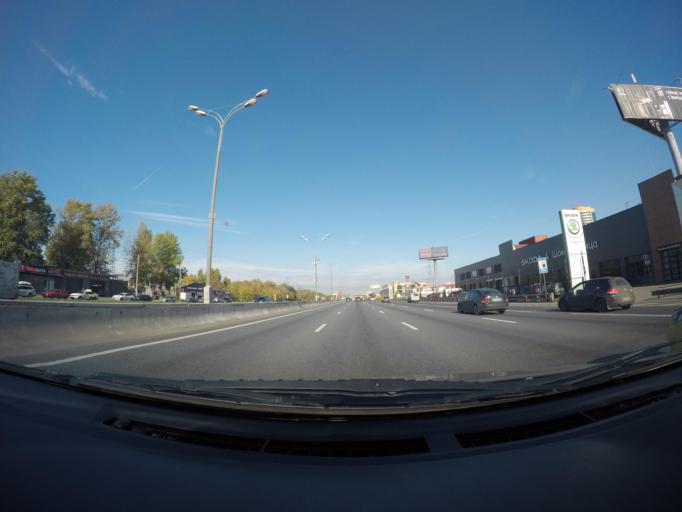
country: RU
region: Moscow
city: Ivanovskoye
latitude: 55.7575
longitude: 37.8427
